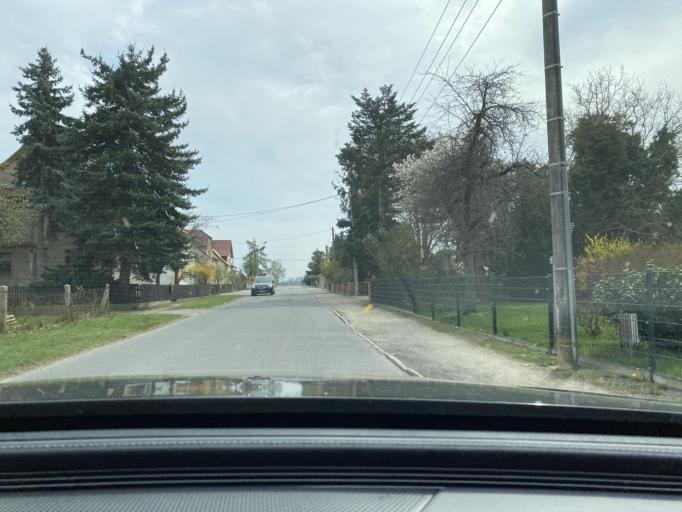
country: DE
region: Saxony
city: Neschwitz
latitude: 51.2657
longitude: 14.3298
